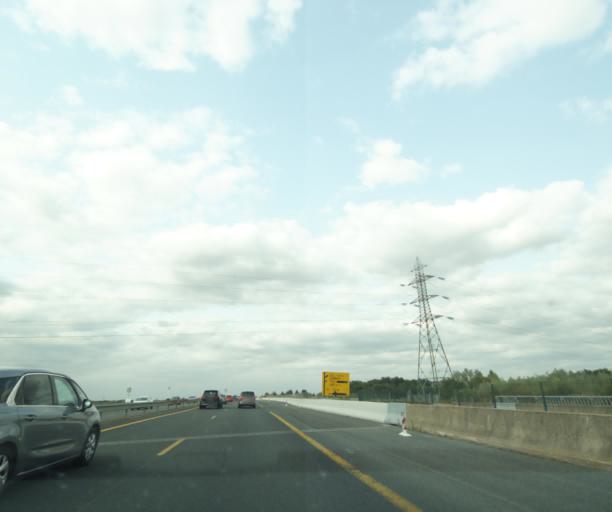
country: FR
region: Centre
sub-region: Departement d'Indre-et-Loire
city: Chambray-les-Tours
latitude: 47.3229
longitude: 0.6909
